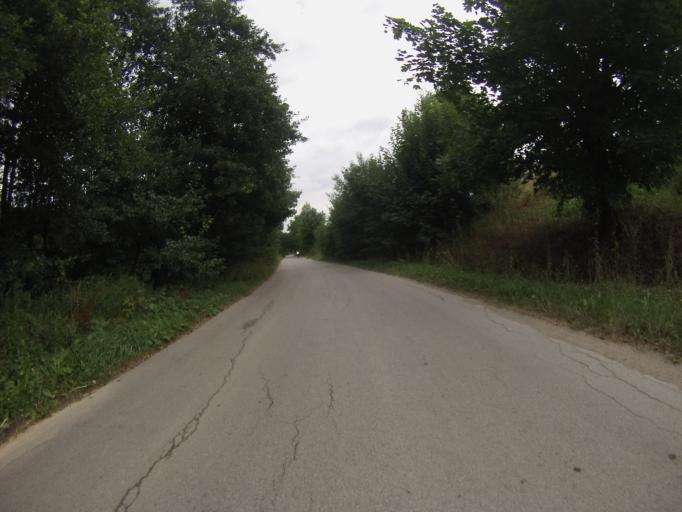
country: PL
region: Swietokrzyskie
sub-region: Powiat kielecki
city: Lagow
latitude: 50.7222
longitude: 21.1100
